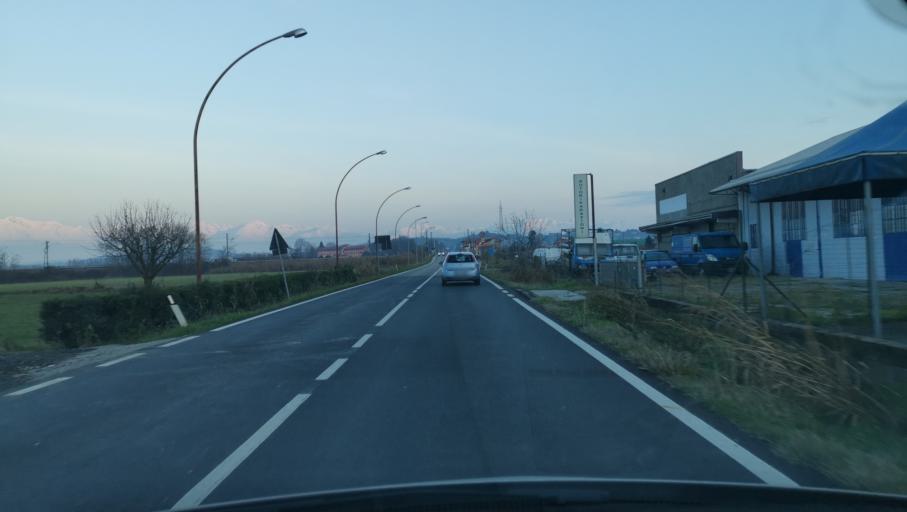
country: IT
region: Piedmont
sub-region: Provincia di Torino
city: Caluso
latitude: 45.2899
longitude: 7.8919
